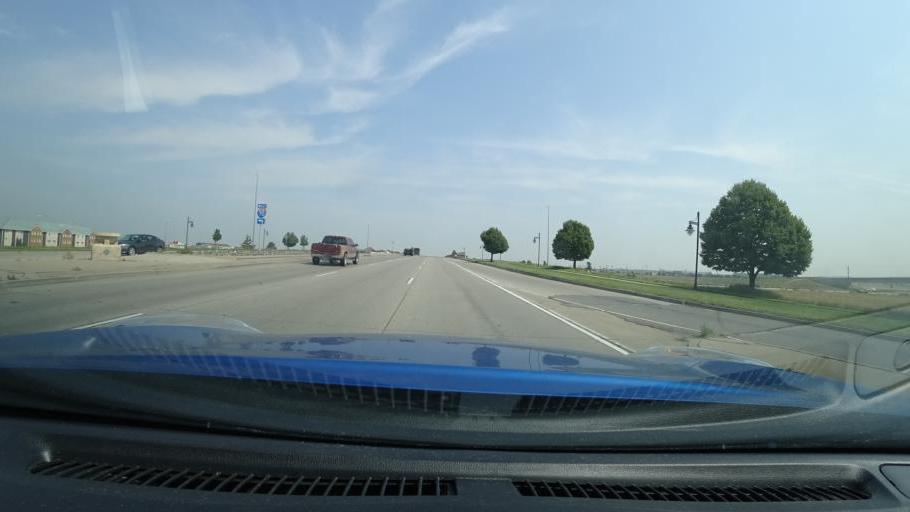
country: US
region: Colorado
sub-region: Adams County
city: Aurora
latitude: 39.7639
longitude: -104.7910
